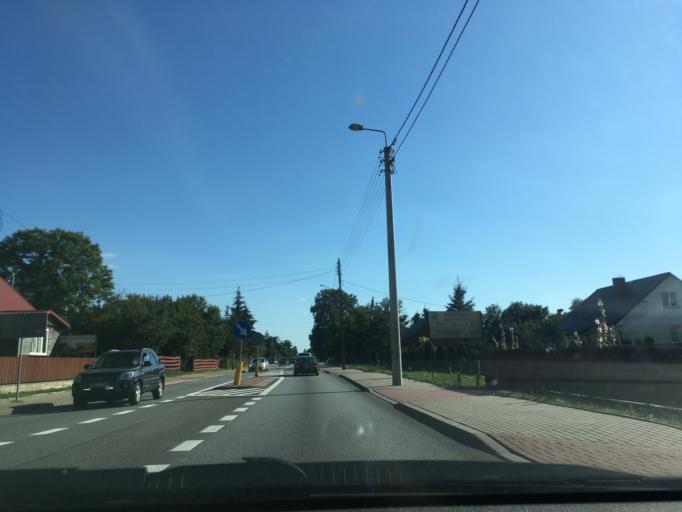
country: PL
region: Podlasie
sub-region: Powiat sokolski
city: Suchowola
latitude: 53.5018
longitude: 23.0976
